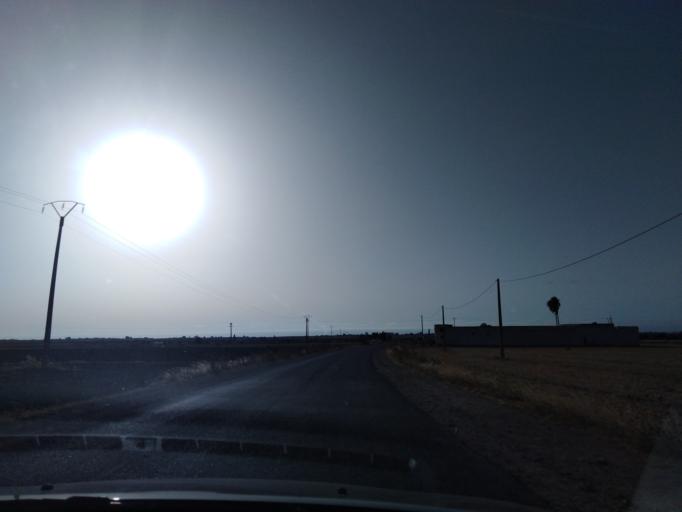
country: MA
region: Doukkala-Abda
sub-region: Safi
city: Safi
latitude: 32.4929
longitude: -8.9281
